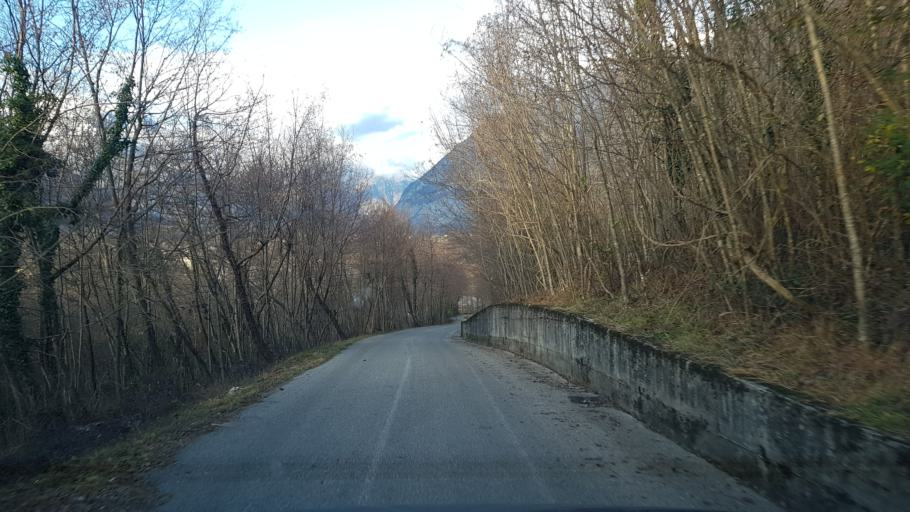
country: IT
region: Friuli Venezia Giulia
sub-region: Provincia di Udine
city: Venzone
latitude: 46.3239
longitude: 13.1412
